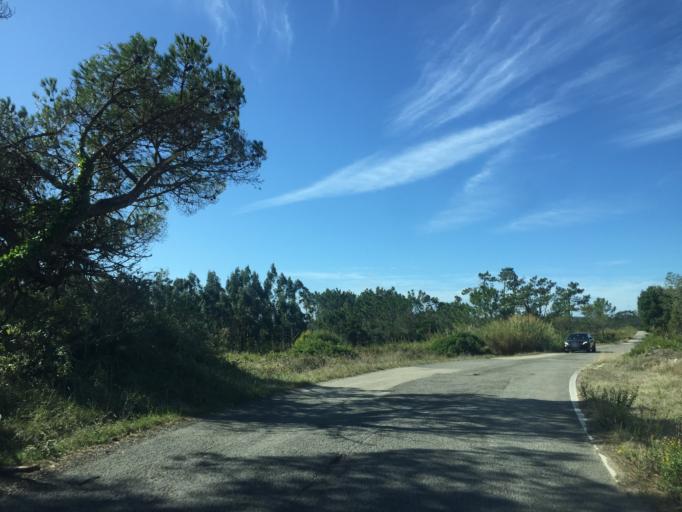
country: PT
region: Coimbra
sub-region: Figueira da Foz
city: Tavarede
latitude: 40.1954
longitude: -8.8537
